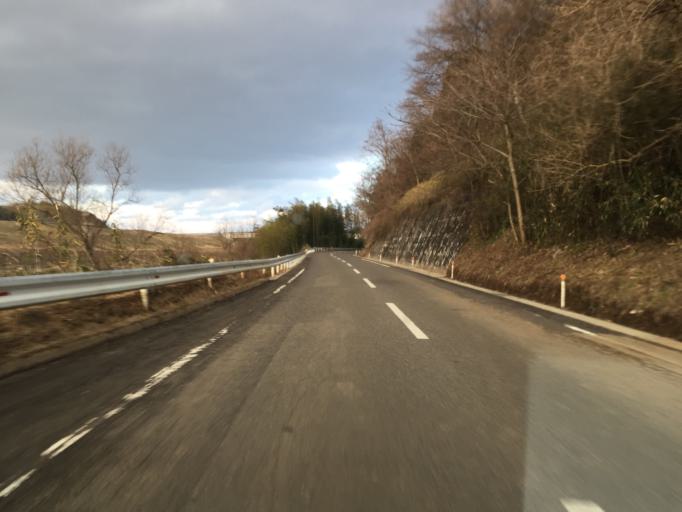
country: JP
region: Fukushima
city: Nihommatsu
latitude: 37.5510
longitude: 140.4329
